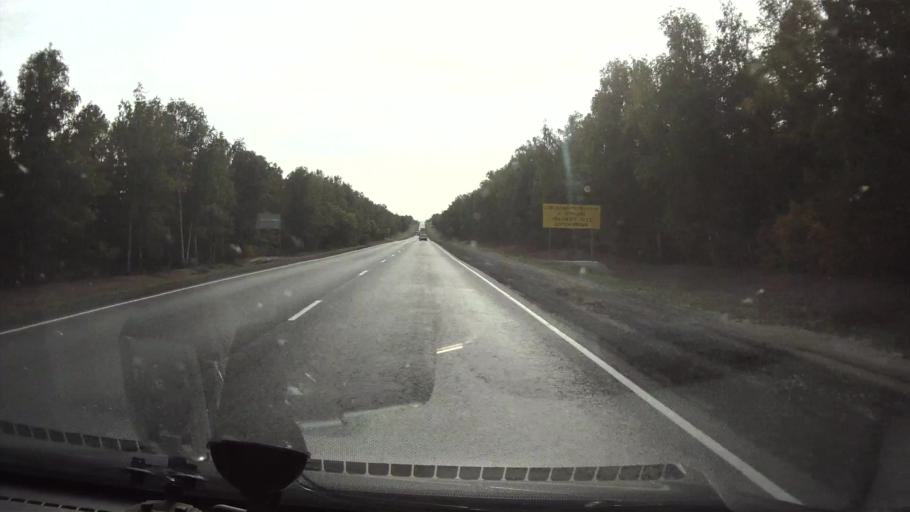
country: RU
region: Saratov
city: Sennoy
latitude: 52.1280
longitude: 46.8570
